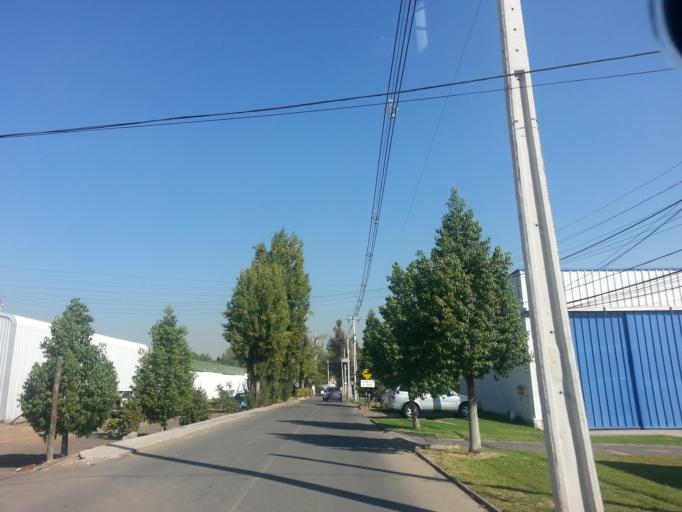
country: CL
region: Santiago Metropolitan
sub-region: Provincia de Santiago
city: Villa Presidente Frei, Nunoa, Santiago, Chile
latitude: -33.4608
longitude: -70.5504
